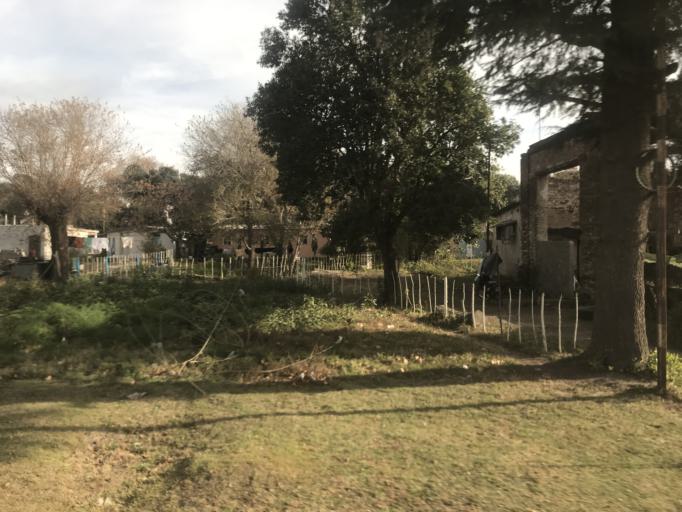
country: AR
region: Cordoba
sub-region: Departamento de Rio Segundo
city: Rio Segundo
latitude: -31.6519
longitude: -63.9120
